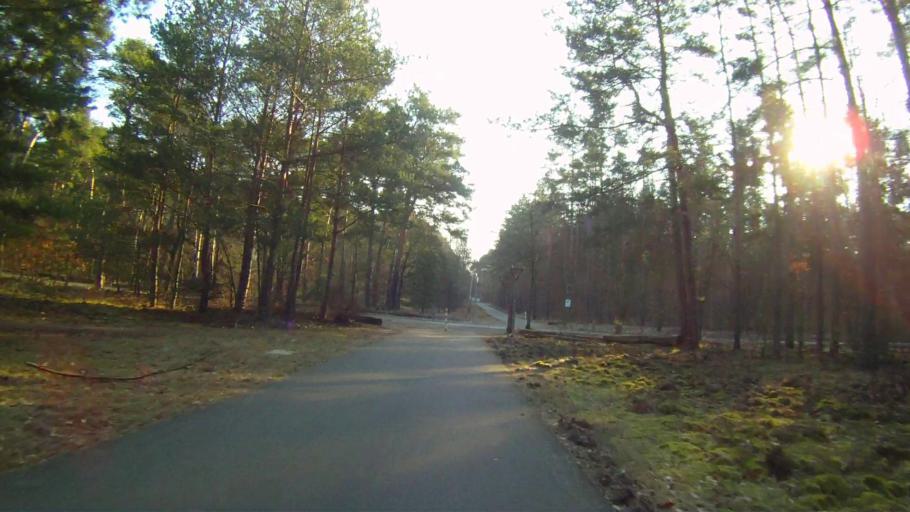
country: DE
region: Berlin
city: Muggelheim
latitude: 52.4247
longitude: 13.6417
